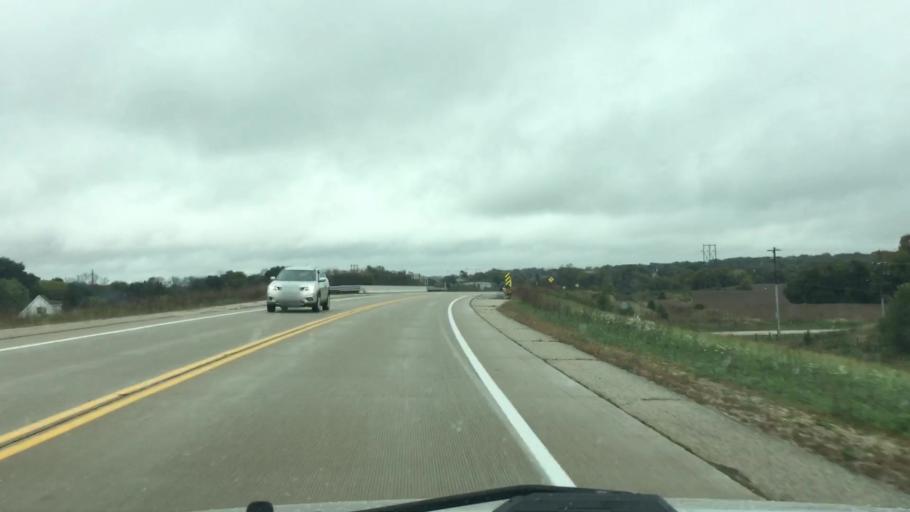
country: US
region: Wisconsin
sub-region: Walworth County
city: Whitewater
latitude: 42.8175
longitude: -88.7367
